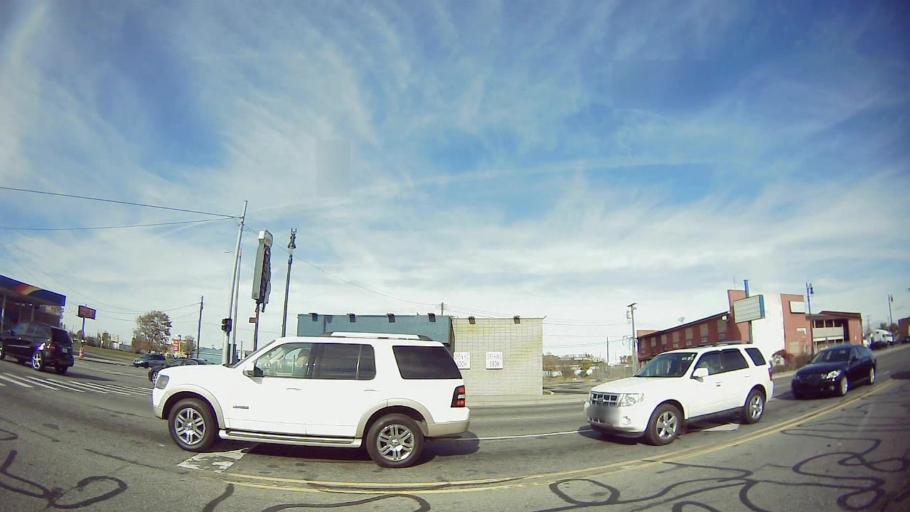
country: US
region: Michigan
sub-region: Wayne County
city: Dearborn
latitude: 42.3278
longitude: -83.1563
